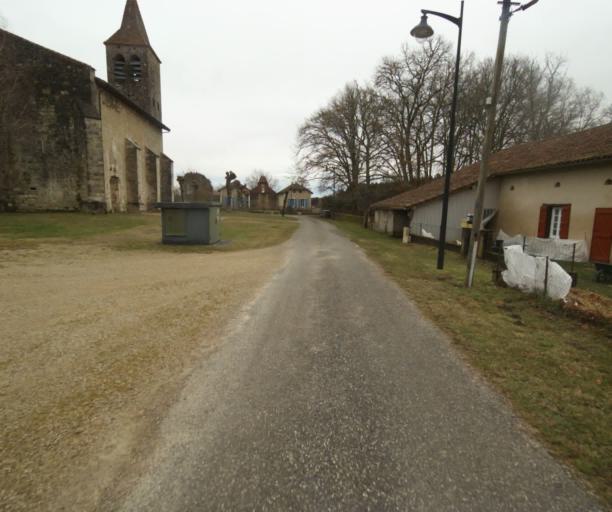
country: FR
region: Aquitaine
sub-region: Departement des Landes
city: Gabarret
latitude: 44.0080
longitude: -0.0253
